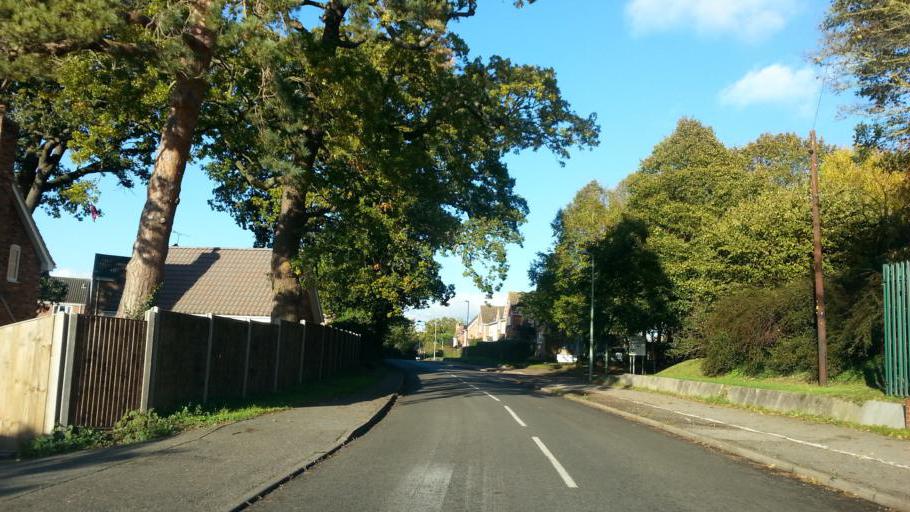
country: GB
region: England
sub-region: Suffolk
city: Thurston
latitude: 52.2511
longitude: 0.8104
